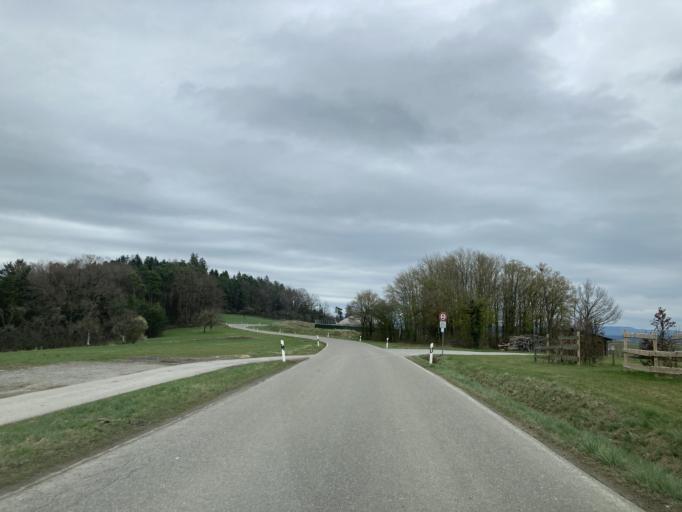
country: DE
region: Baden-Wuerttemberg
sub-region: Regierungsbezirk Stuttgart
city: Bondorf
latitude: 48.4846
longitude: 8.8498
